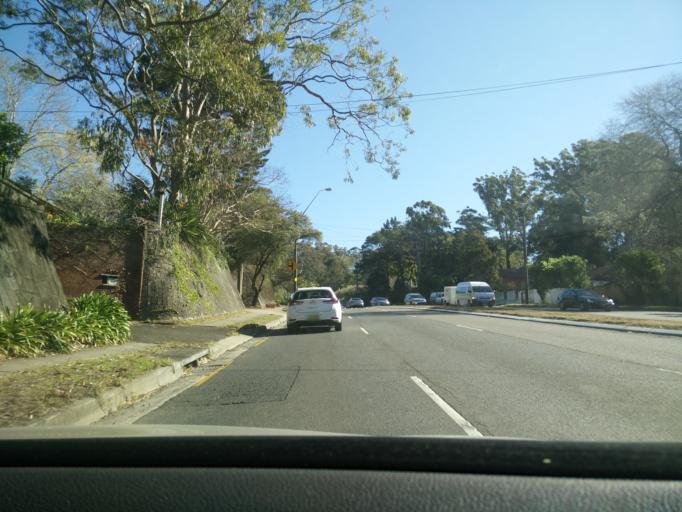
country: AU
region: New South Wales
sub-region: City of Sydney
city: Pymble
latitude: -33.7553
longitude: 151.1393
